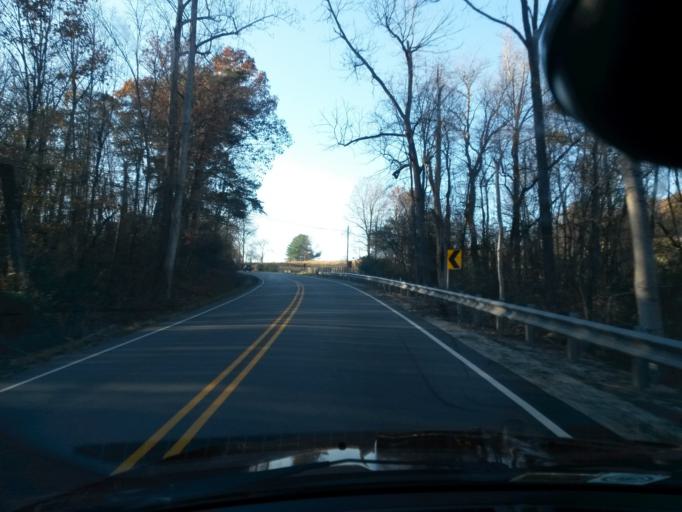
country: US
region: Virginia
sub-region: Amherst County
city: Amherst
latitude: 37.6225
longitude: -79.1077
